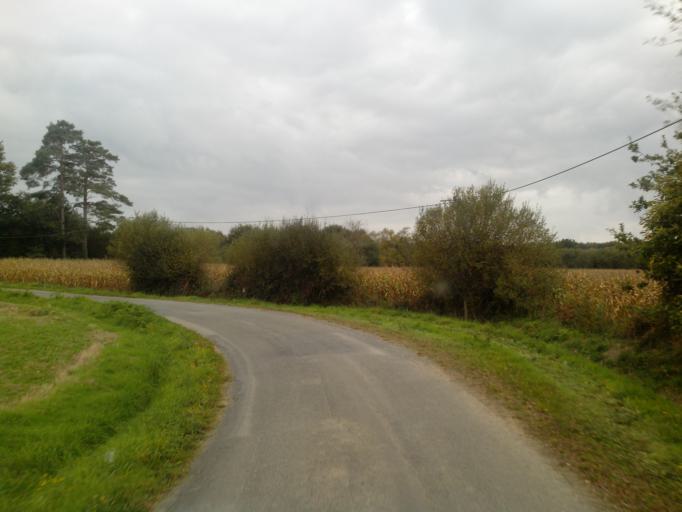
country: FR
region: Brittany
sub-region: Departement du Morbihan
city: Meneac
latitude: 48.1167
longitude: -2.3933
